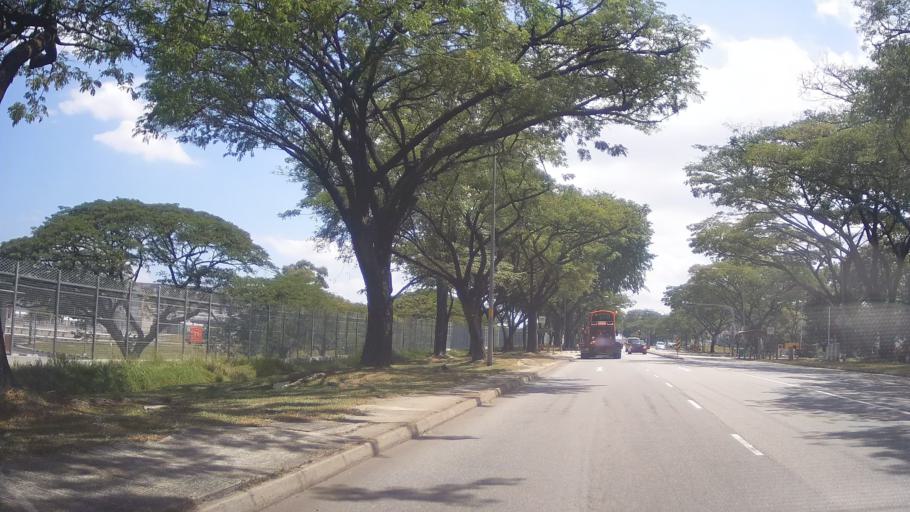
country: SG
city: Singapore
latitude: 1.3122
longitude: 103.6852
